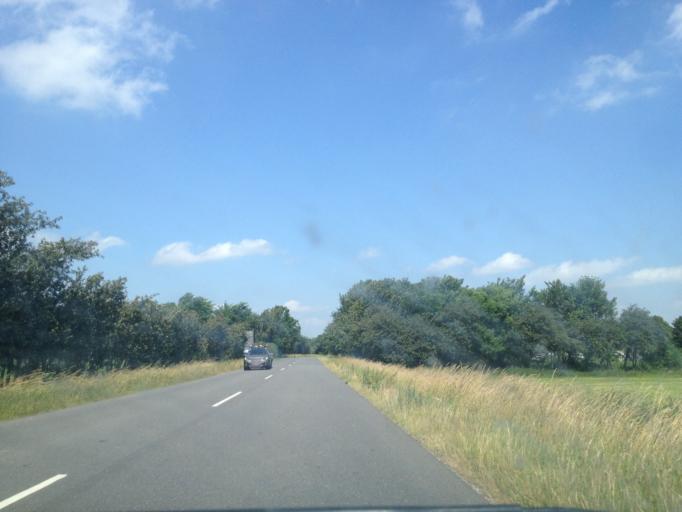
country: DK
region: South Denmark
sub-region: Kolding Kommune
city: Vamdrup
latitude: 55.4002
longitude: 9.2402
